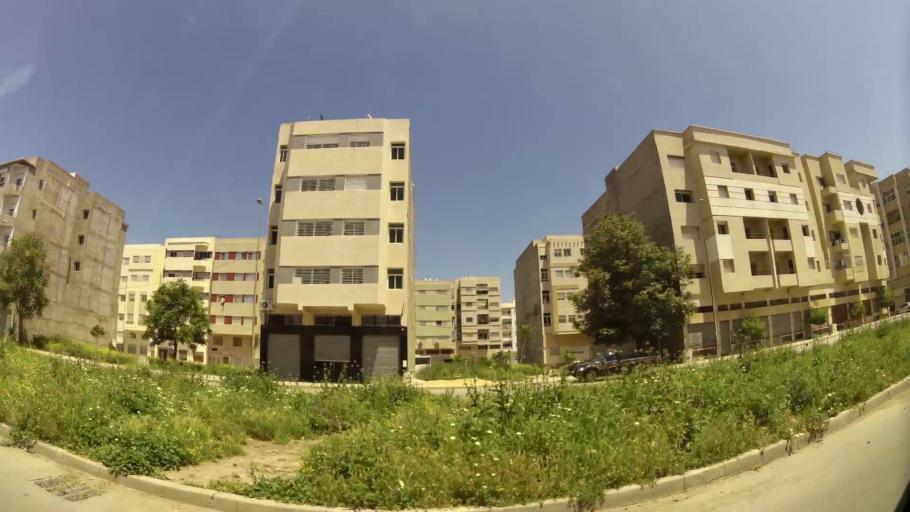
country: MA
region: Fes-Boulemane
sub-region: Fes
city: Fes
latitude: 34.0311
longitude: -5.0435
